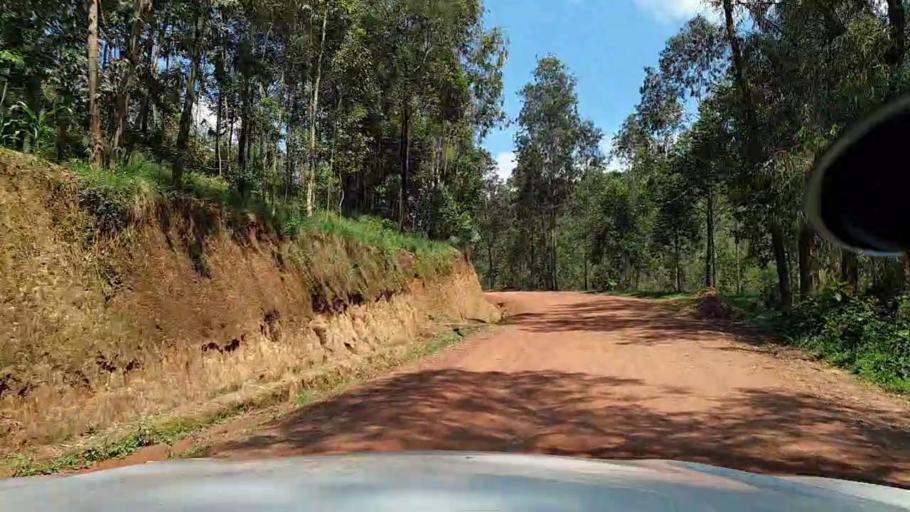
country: RW
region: Kigali
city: Kigali
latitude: -1.7633
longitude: 29.8723
